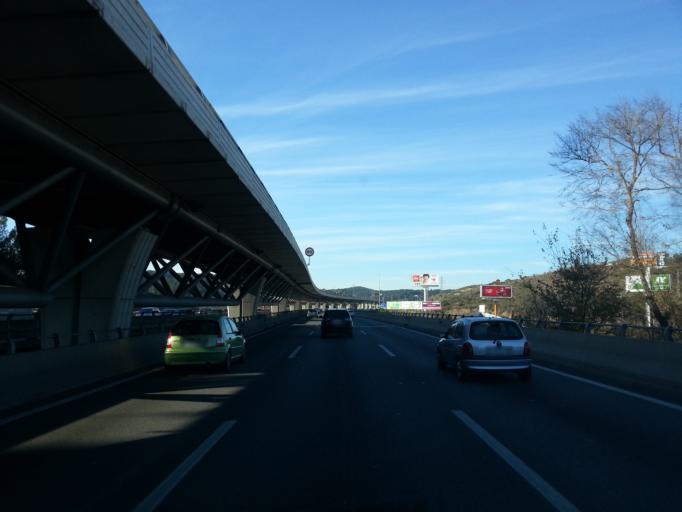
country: ES
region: Catalonia
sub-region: Provincia de Barcelona
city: Montcada i Reixac
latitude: 41.4638
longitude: 2.1790
